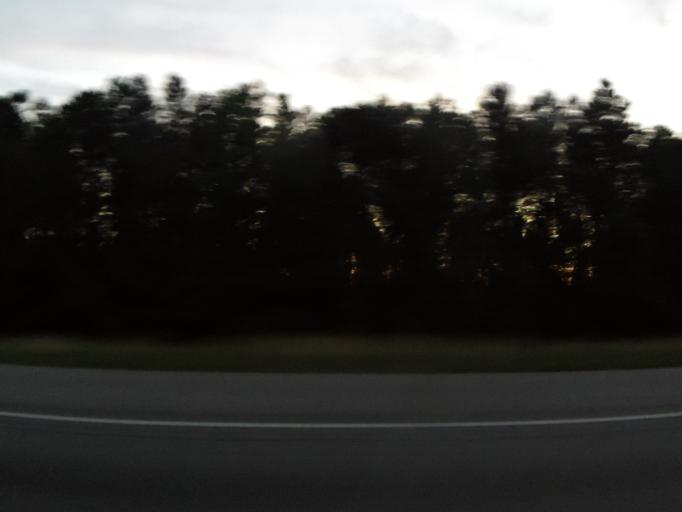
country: US
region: Georgia
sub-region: Liberty County
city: Midway
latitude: 31.7501
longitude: -81.3844
